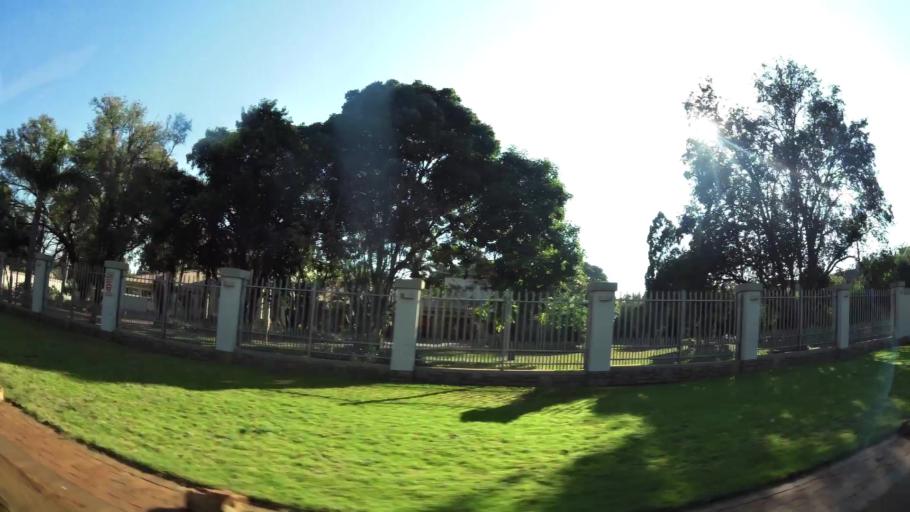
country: ZA
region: Gauteng
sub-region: City of Tshwane Metropolitan Municipality
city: Pretoria
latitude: -25.6723
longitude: 28.2067
